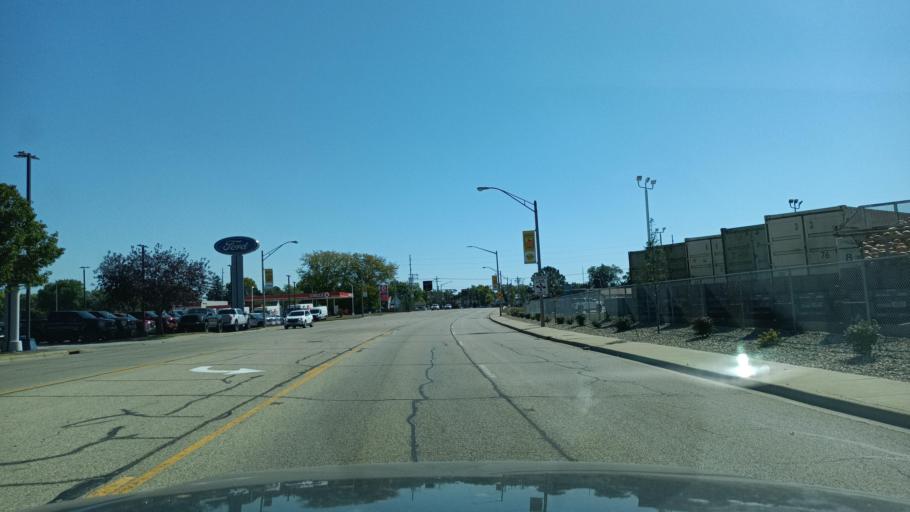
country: US
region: Illinois
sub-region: Tazewell County
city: Morton
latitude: 40.6155
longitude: -89.4635
